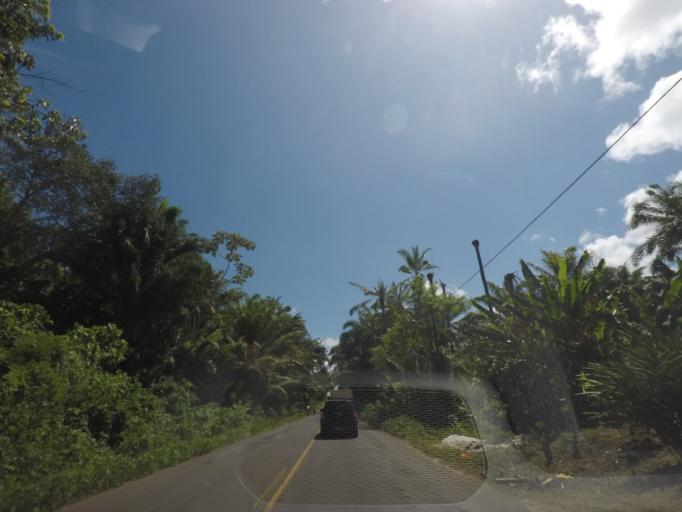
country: BR
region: Bahia
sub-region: Valenca
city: Valenca
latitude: -13.4504
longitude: -39.0860
